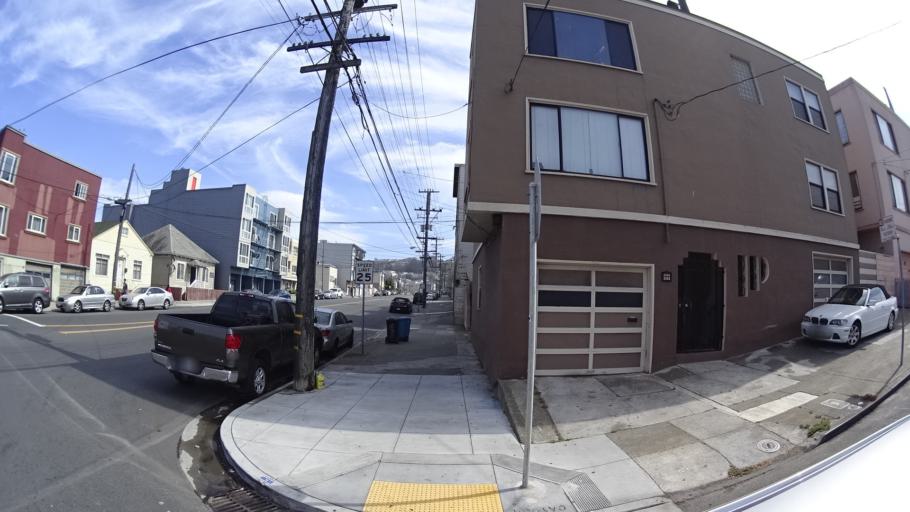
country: US
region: California
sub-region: San Mateo County
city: Daly City
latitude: 37.7102
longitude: -122.4547
